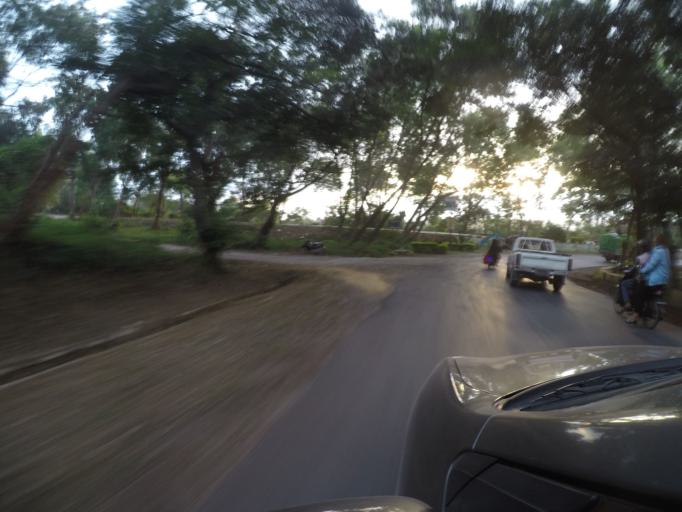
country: MM
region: Shan
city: Taunggyi
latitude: 20.7918
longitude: 97.0157
